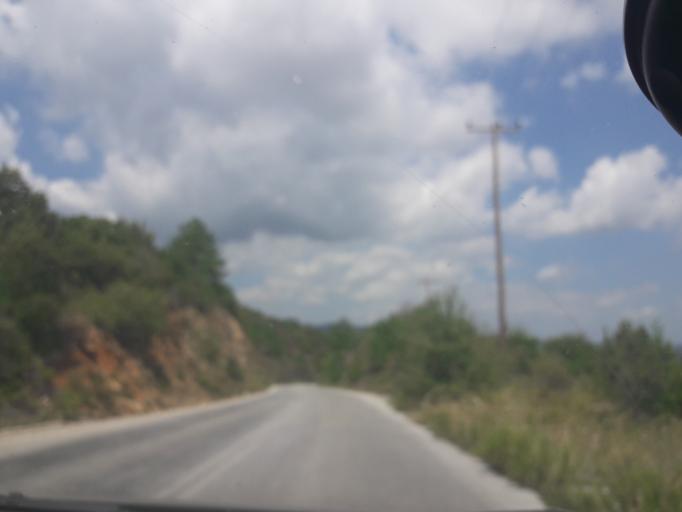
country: GR
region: Central Macedonia
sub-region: Nomos Chalkidikis
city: Polygyros
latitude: 40.3536
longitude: 23.4897
